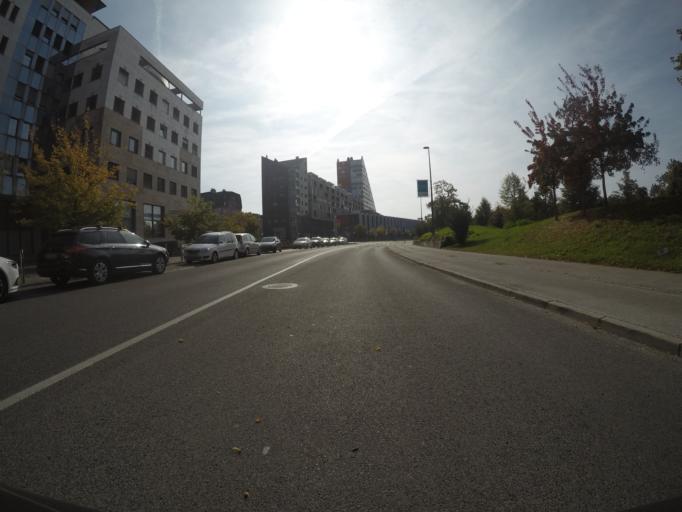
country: SI
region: Ljubljana
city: Ljubljana
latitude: 46.0624
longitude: 14.5133
